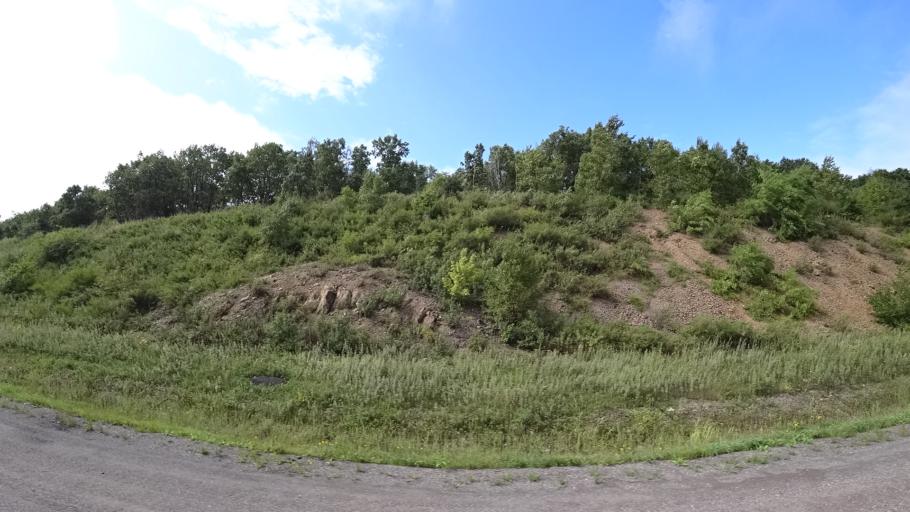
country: RU
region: Primorskiy
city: Lyalichi
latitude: 44.1232
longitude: 132.4220
